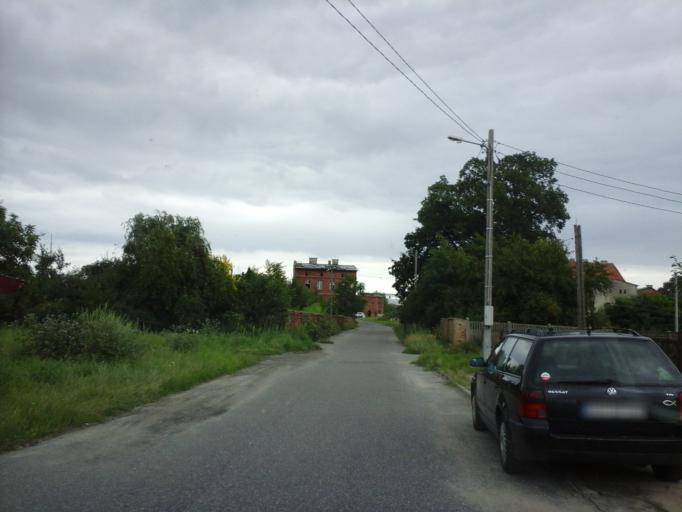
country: PL
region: West Pomeranian Voivodeship
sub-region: Powiat choszczenski
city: Krzecin
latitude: 53.0549
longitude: 15.4780
